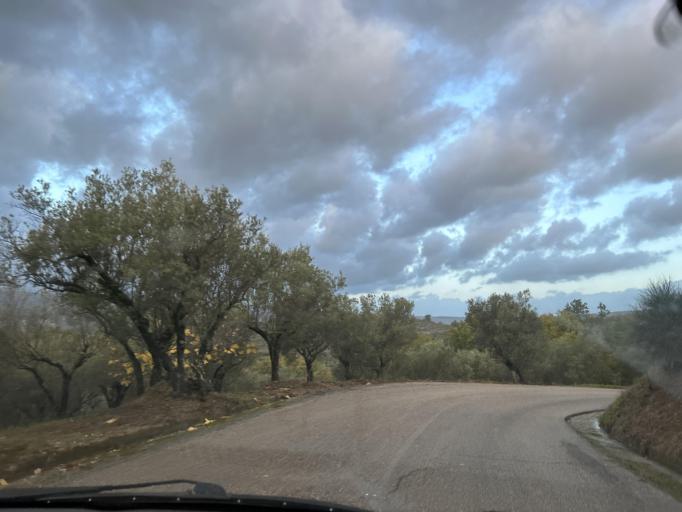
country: IT
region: Calabria
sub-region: Provincia di Catanzaro
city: Squillace
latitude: 38.7718
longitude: 16.5093
